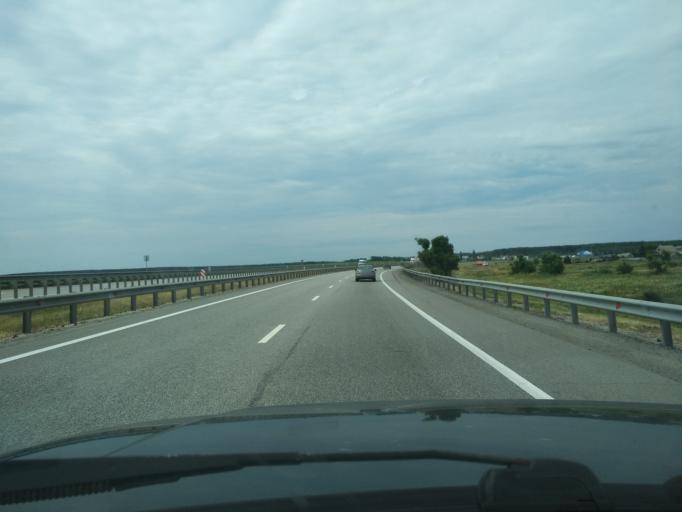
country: RU
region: Lipetsk
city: Khlevnoye
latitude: 52.0661
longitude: 39.1799
